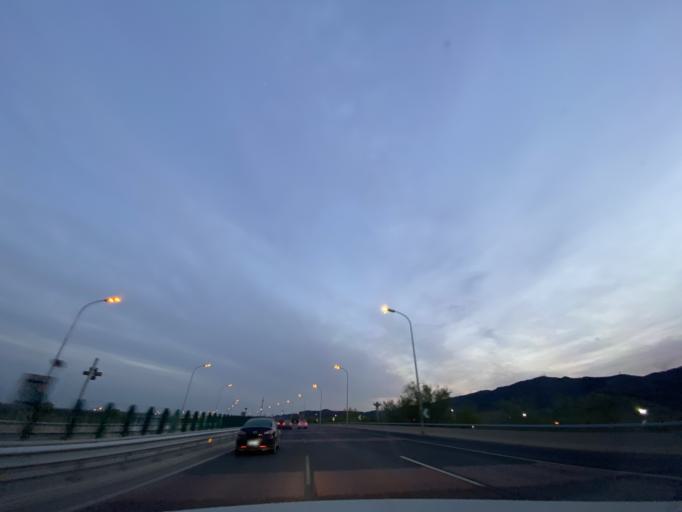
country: CN
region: Beijing
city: Xiangshan
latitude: 39.9911
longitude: 116.2160
